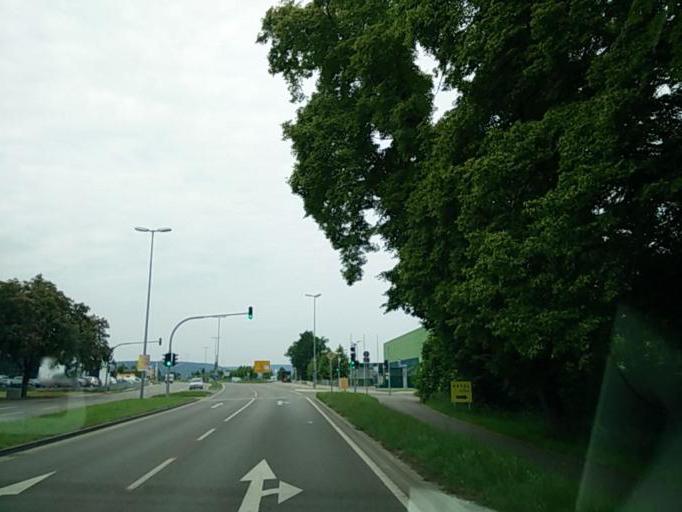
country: DE
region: Baden-Wuerttemberg
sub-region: Tuebingen Region
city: Tuebingen
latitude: 48.5109
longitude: 9.0436
